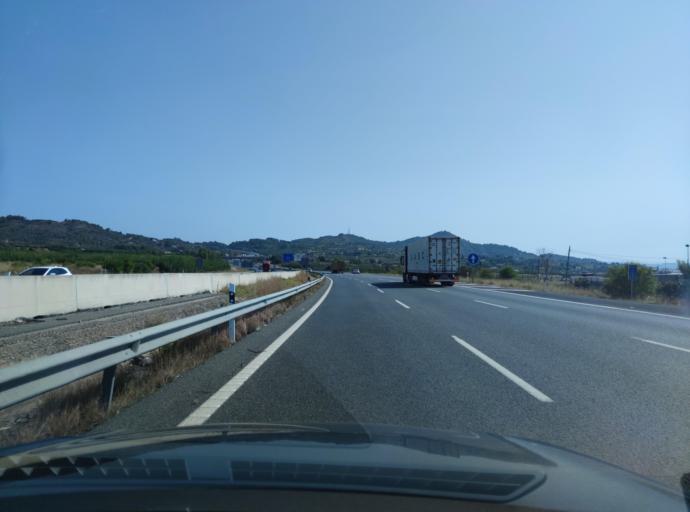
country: ES
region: Valencia
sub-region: Provincia de Valencia
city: Rotgla y Corbera
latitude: 39.0120
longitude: -0.5617
